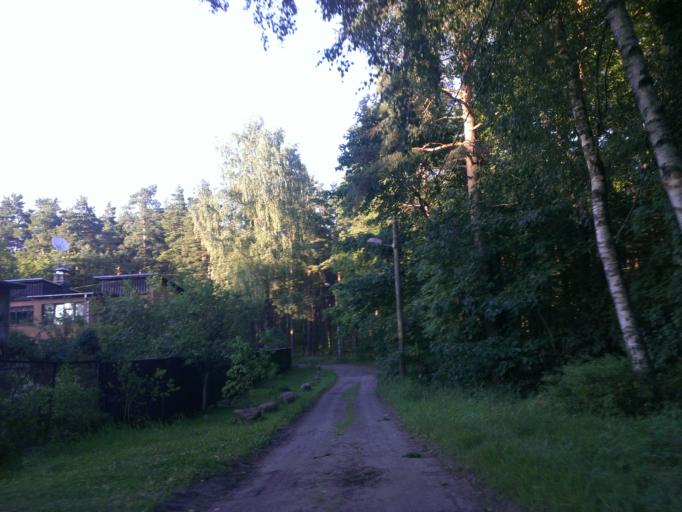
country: LV
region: Riga
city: Bergi
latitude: 56.9826
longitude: 24.3073
